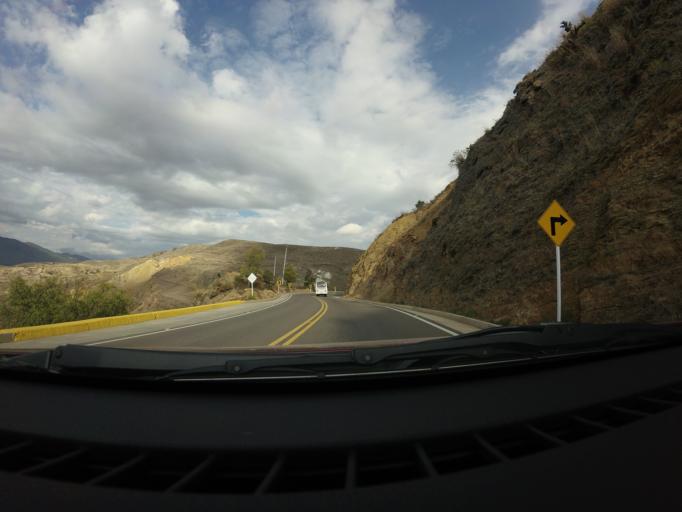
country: CO
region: Boyaca
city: Sachica
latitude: 5.5640
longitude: -73.5008
